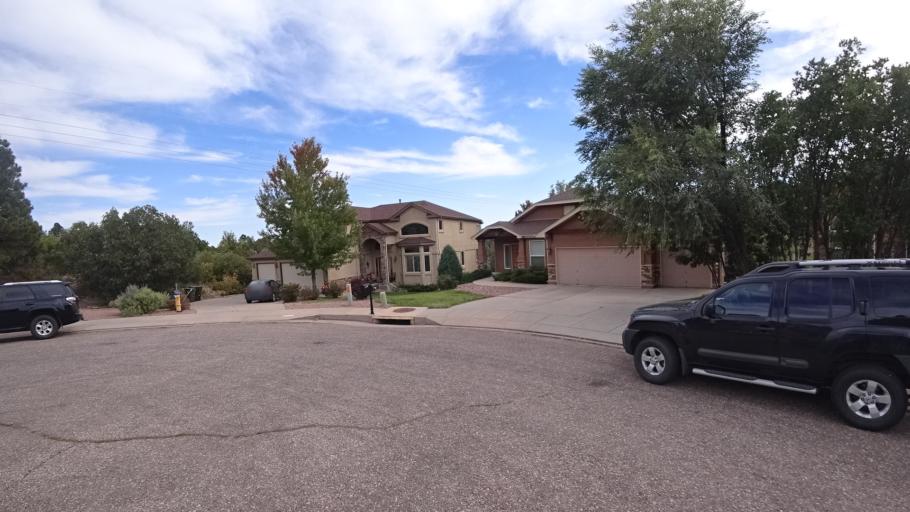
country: US
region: Colorado
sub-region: El Paso County
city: Colorado Springs
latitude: 38.9024
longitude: -104.7854
